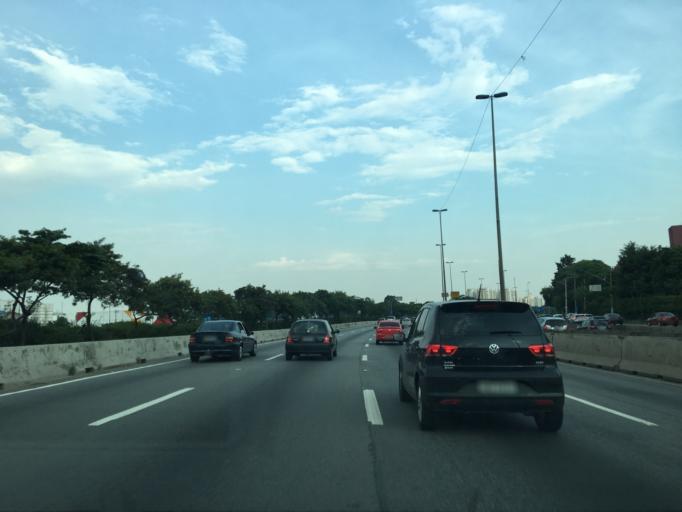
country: BR
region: Sao Paulo
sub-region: Sao Paulo
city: Sao Paulo
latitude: -23.5194
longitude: -46.6179
